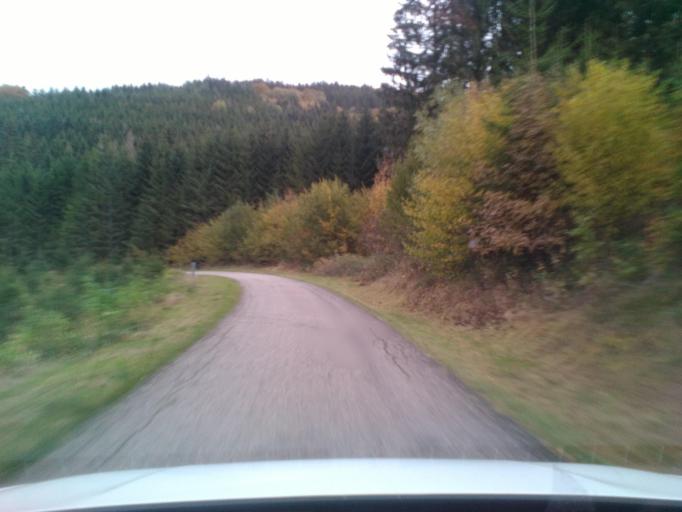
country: FR
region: Lorraine
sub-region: Departement des Vosges
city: Senones
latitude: 48.3743
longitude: 7.0777
